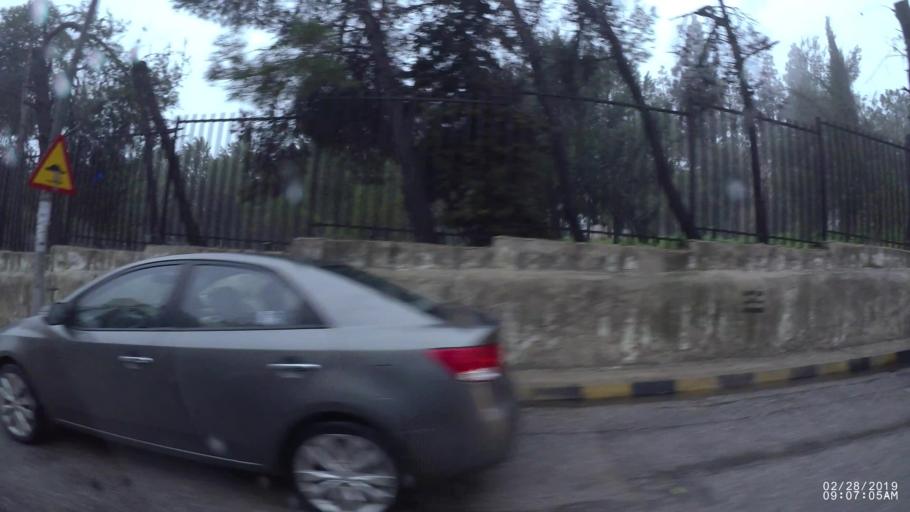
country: JO
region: Amman
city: Al Jubayhah
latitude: 32.0156
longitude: 35.8759
